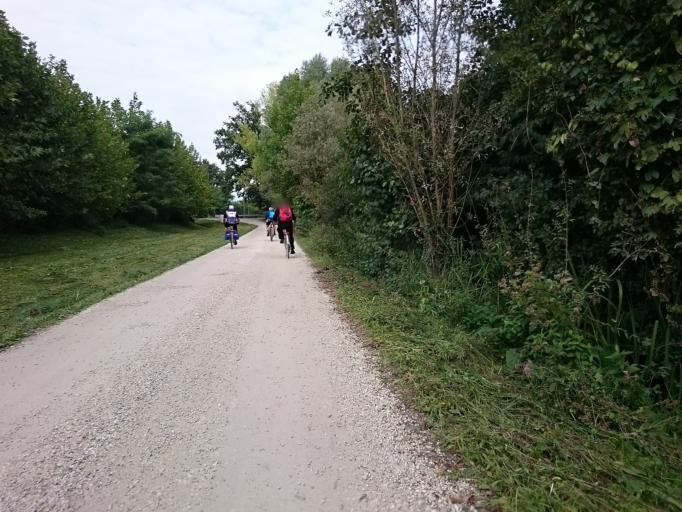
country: IT
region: Veneto
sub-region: Provincia di Vicenza
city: Quinto Vicentino
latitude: 45.5753
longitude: 11.6596
